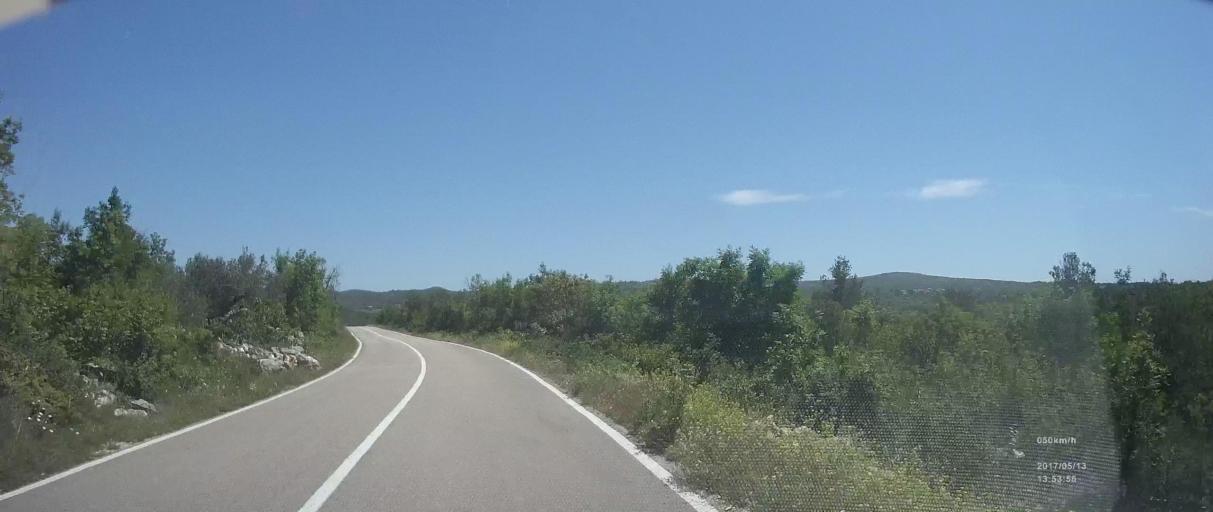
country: HR
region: Sibensko-Kniniska
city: Rogoznica
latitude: 43.5972
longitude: 16.0029
